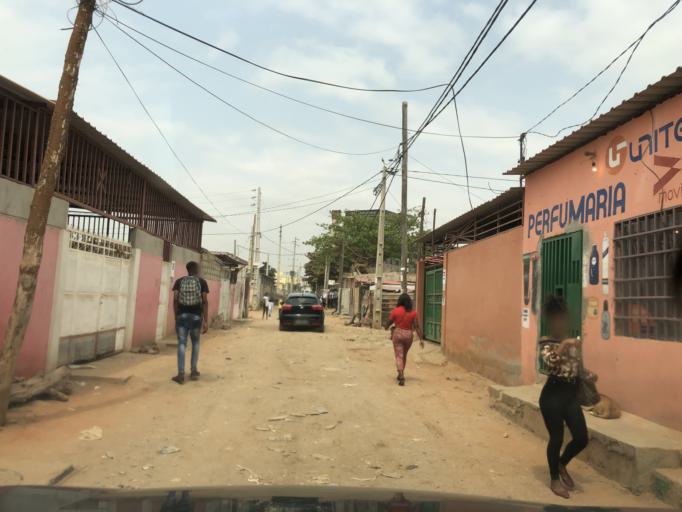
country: AO
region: Luanda
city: Luanda
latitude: -8.9123
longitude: 13.1741
